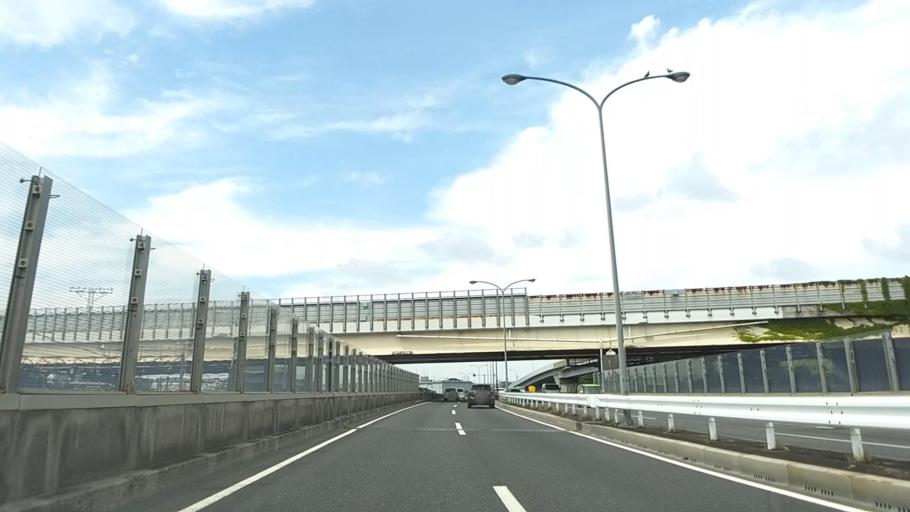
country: JP
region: Kanagawa
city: Yokohama
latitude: 35.4871
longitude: 139.5935
